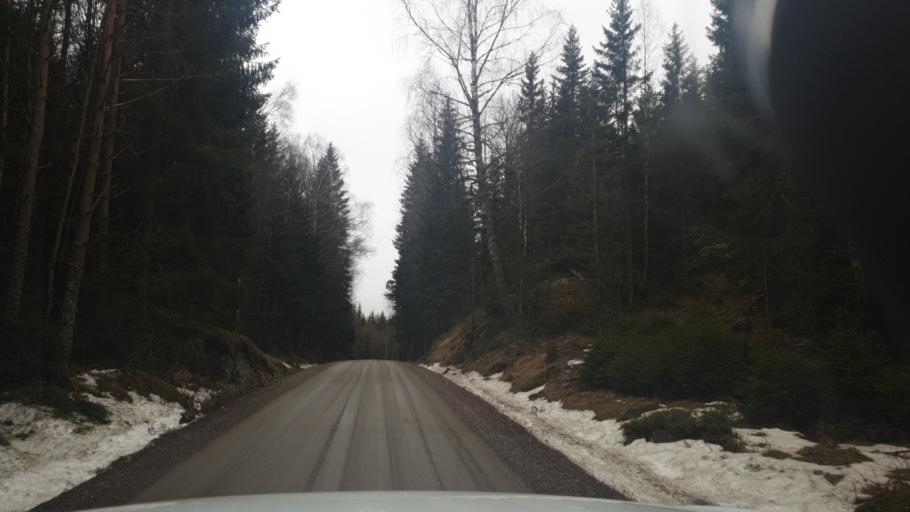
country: NO
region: Ostfold
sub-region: Romskog
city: Romskog
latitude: 59.7158
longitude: 11.9872
